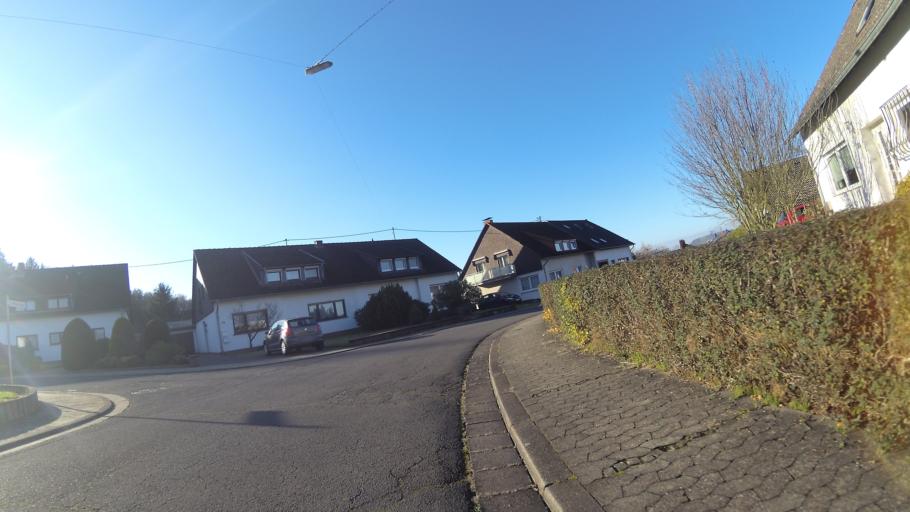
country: DE
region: Saarland
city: Schwalbach
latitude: 49.2952
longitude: 6.8224
